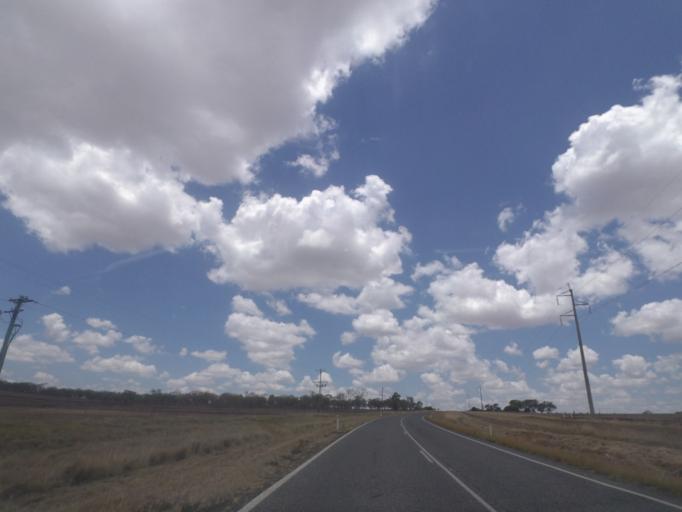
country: AU
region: Queensland
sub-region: Toowoomba
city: Top Camp
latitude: -27.8792
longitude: 151.9691
